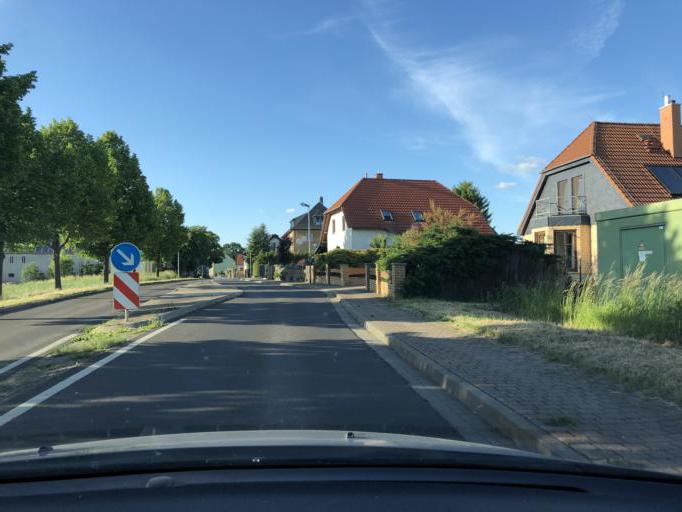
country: DE
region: Saxony
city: Groitzsch
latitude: 51.1693
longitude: 12.2884
